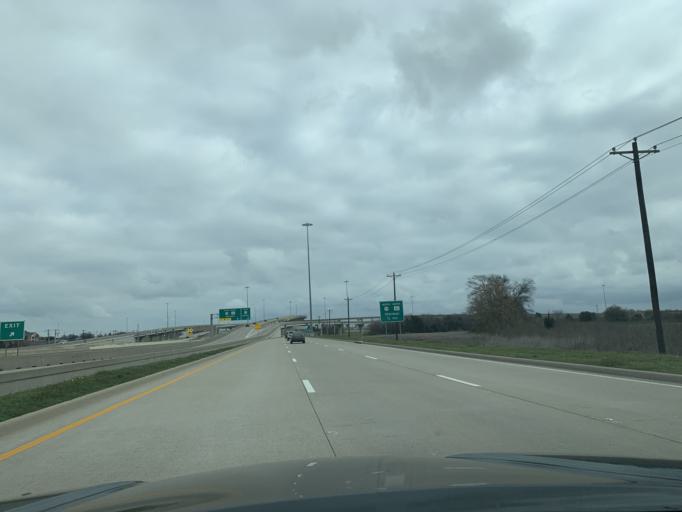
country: US
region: Texas
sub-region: Collin County
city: Fairview
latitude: 33.1535
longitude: -96.6549
